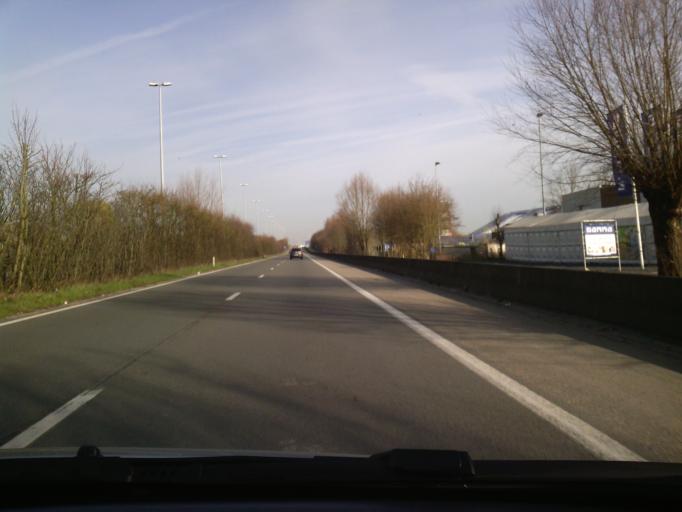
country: FR
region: Nord-Pas-de-Calais
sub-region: Departement du Nord
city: Halluin
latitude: 50.7897
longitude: 3.1389
